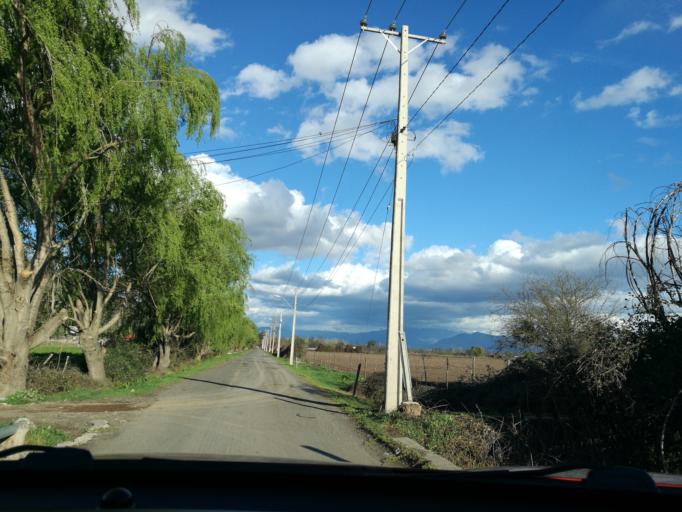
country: CL
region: O'Higgins
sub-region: Provincia de Cachapoal
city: Graneros
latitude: -34.0961
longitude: -70.8177
